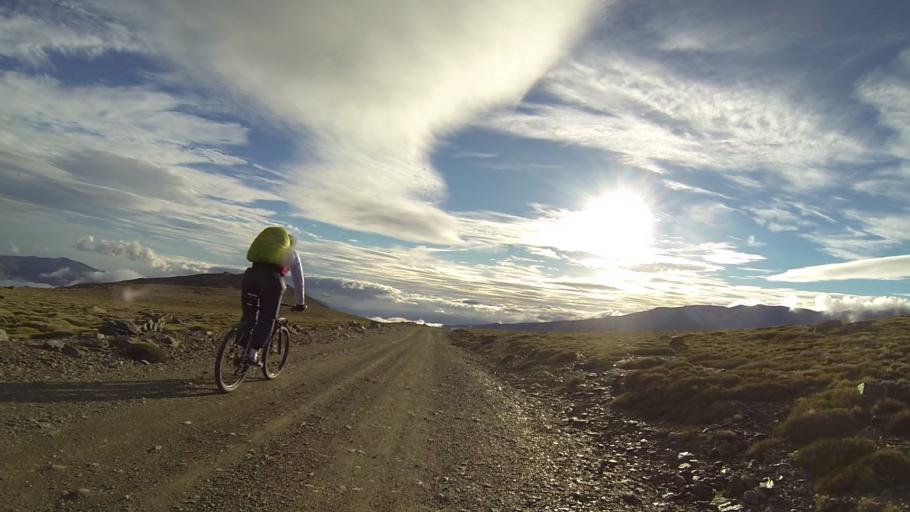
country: ES
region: Andalusia
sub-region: Provincia de Granada
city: Trevelez
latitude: 37.0066
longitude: -3.3061
